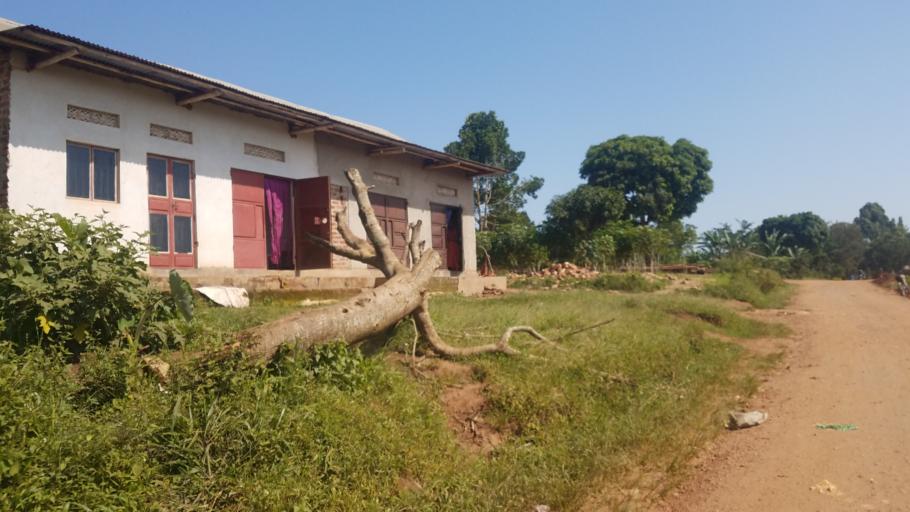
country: UG
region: Central Region
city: Masaka
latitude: -0.3285
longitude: 31.7093
